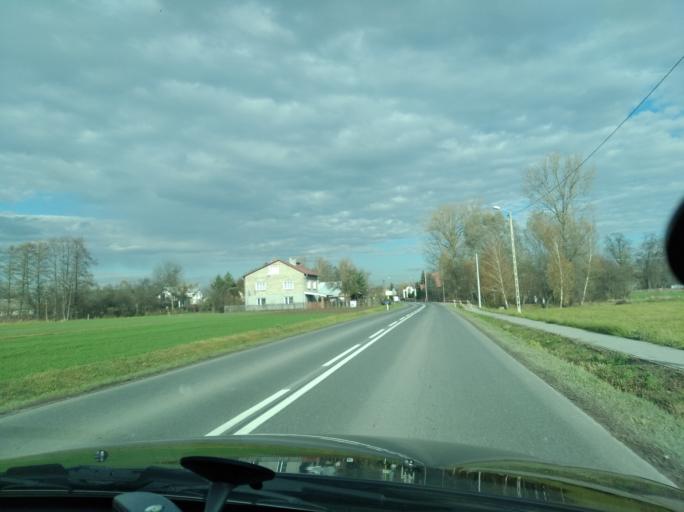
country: PL
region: Subcarpathian Voivodeship
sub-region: Powiat ropczycko-sedziszowski
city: Ostrow
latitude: 50.0943
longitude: 21.5933
